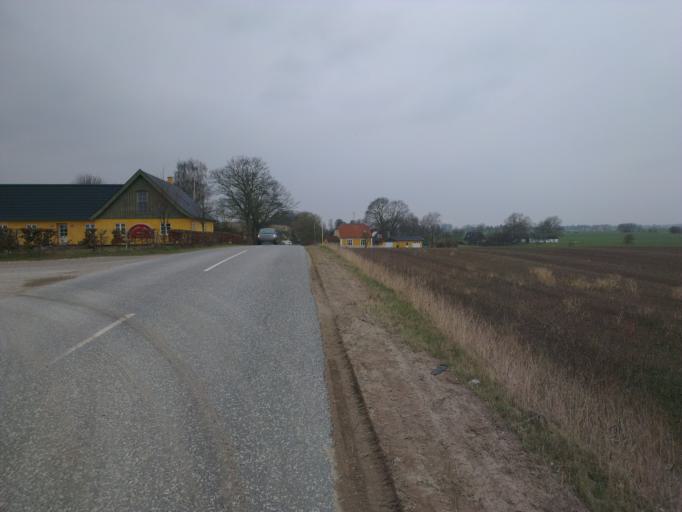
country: DK
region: Capital Region
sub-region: Frederikssund Kommune
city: Frederikssund
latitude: 55.8542
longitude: 12.1224
